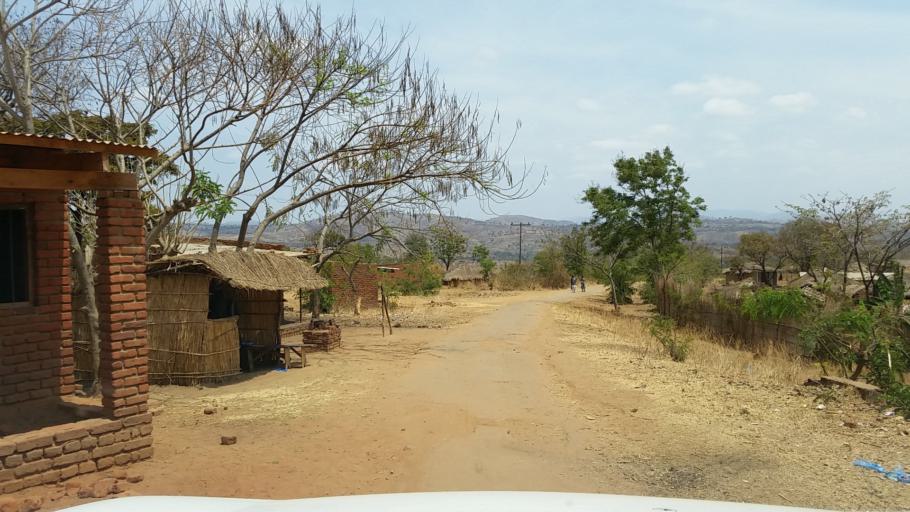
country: MW
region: Central Region
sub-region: Dowa District
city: Dowa
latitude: -13.7203
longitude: 34.1068
